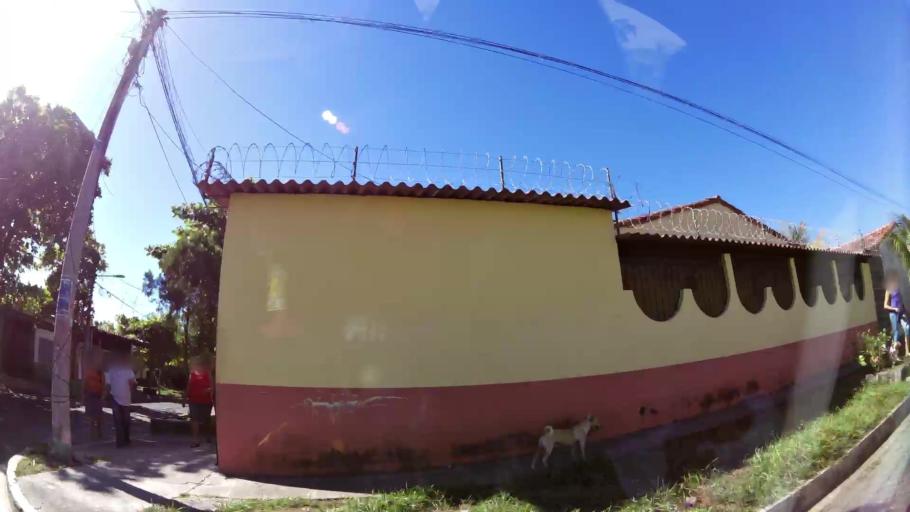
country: SV
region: San Miguel
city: San Miguel
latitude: 13.4708
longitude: -88.1532
